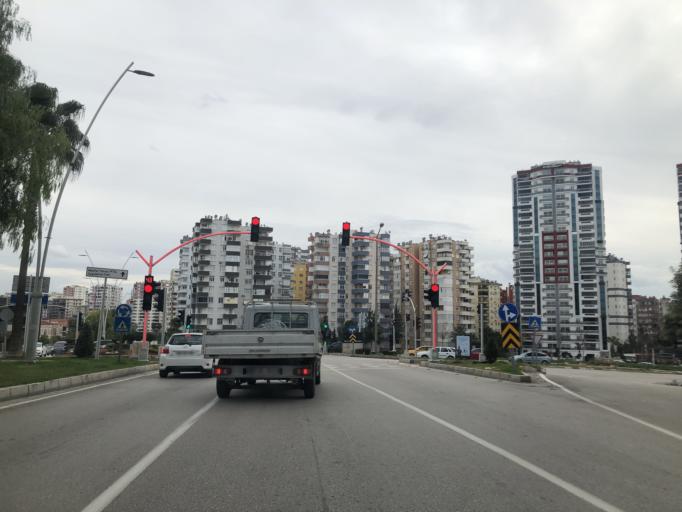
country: TR
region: Adana
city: Adana
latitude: 37.0545
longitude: 35.2878
